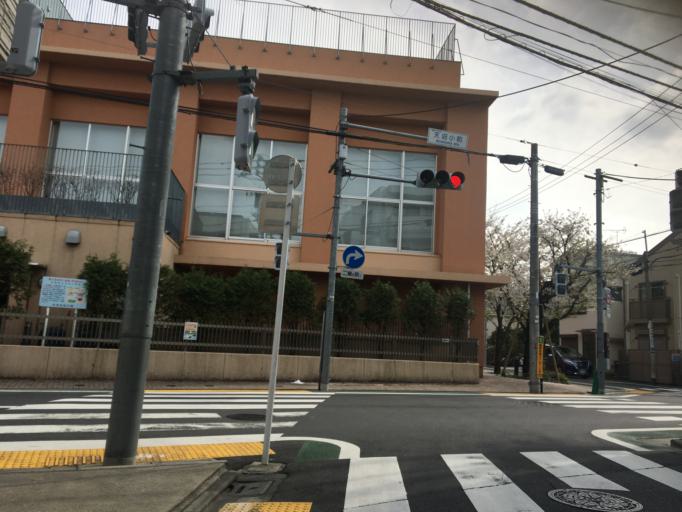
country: JP
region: Tokyo
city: Musashino
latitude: 35.7111
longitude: 139.6228
